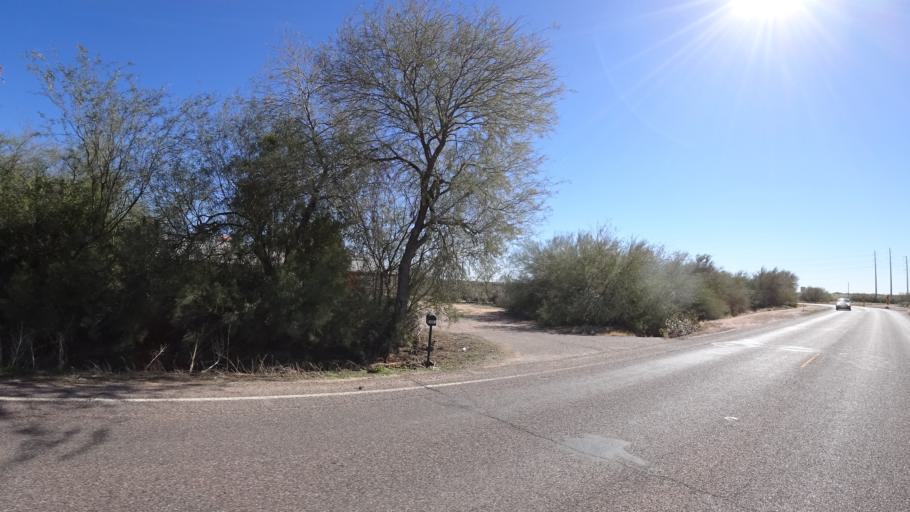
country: US
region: Arizona
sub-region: Maricopa County
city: Mesa
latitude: 33.4864
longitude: -111.8222
